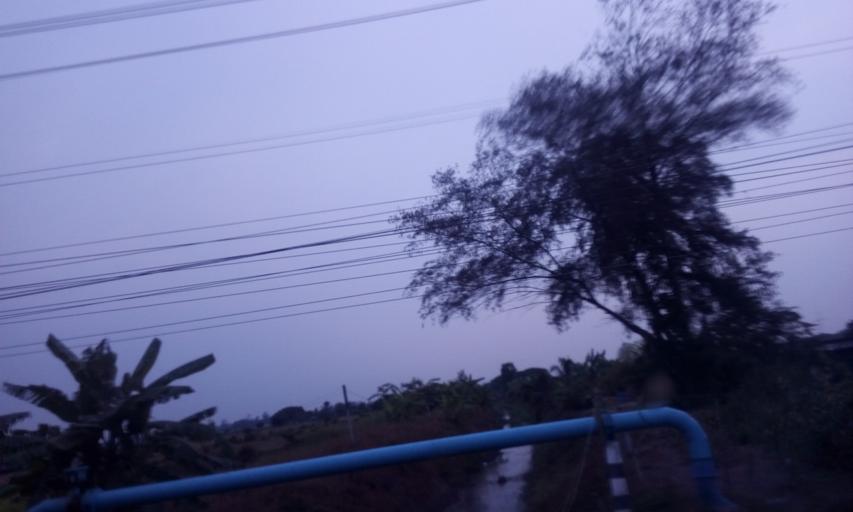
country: TH
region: Bangkok
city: Nong Chok
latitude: 13.8233
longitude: 100.9236
